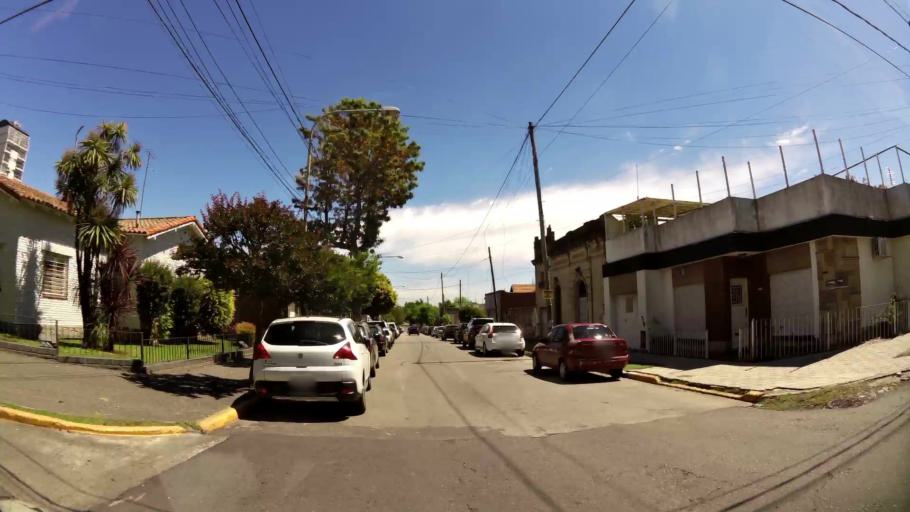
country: AR
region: Buenos Aires
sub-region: Partido de Quilmes
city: Quilmes
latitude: -34.7157
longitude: -58.2556
